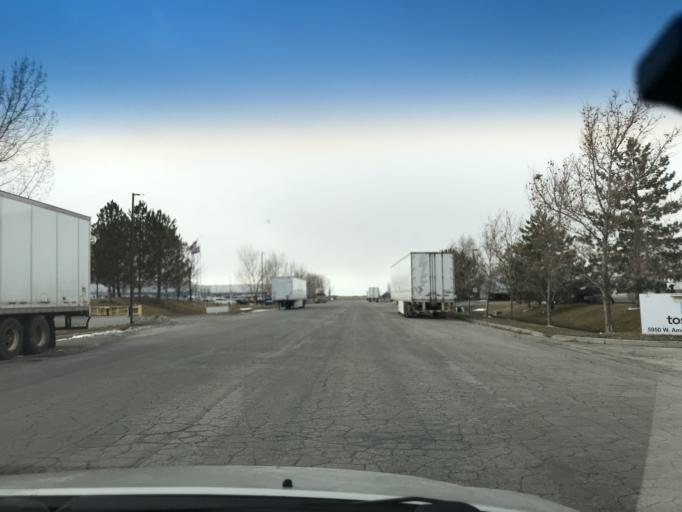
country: US
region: Utah
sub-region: Salt Lake County
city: West Valley City
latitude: 40.7788
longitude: -112.0322
